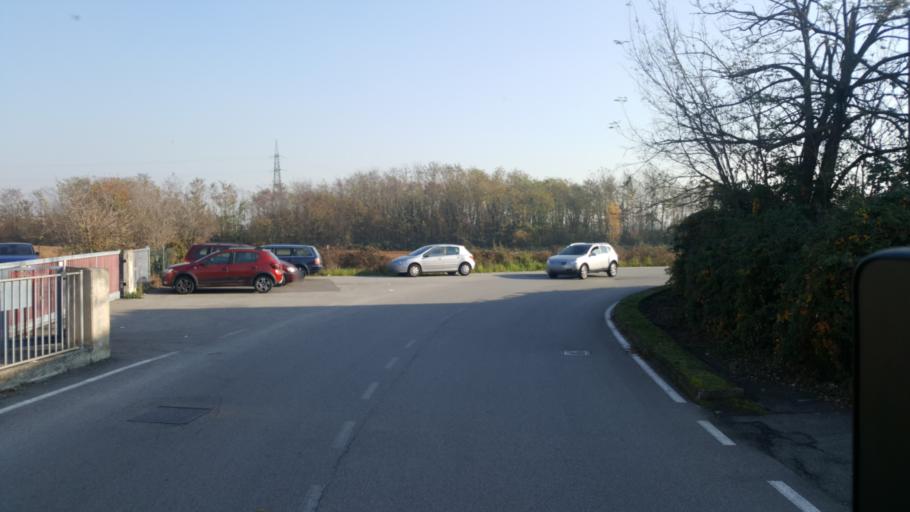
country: IT
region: Lombardy
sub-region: Provincia di Monza e Brianza
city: Bellusco
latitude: 45.6260
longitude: 9.4303
